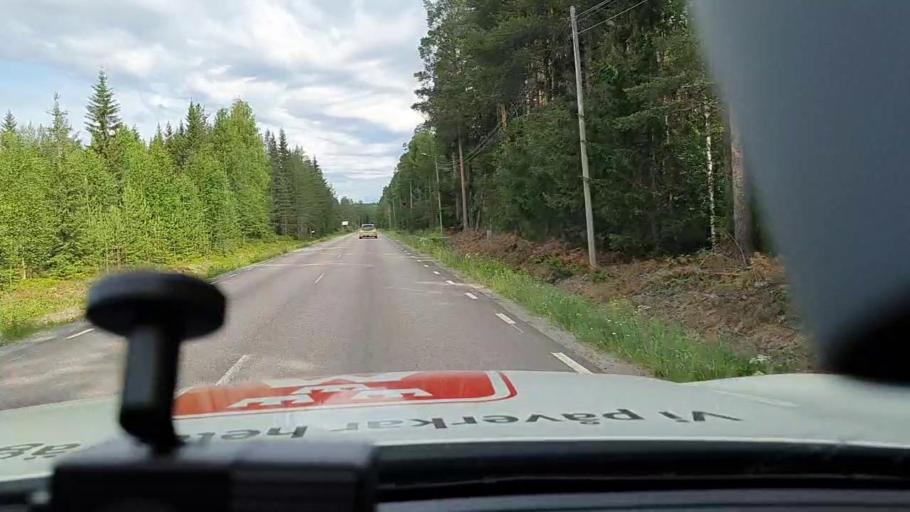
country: SE
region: Norrbotten
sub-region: Bodens Kommun
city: Saevast
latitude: 65.7267
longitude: 21.7463
